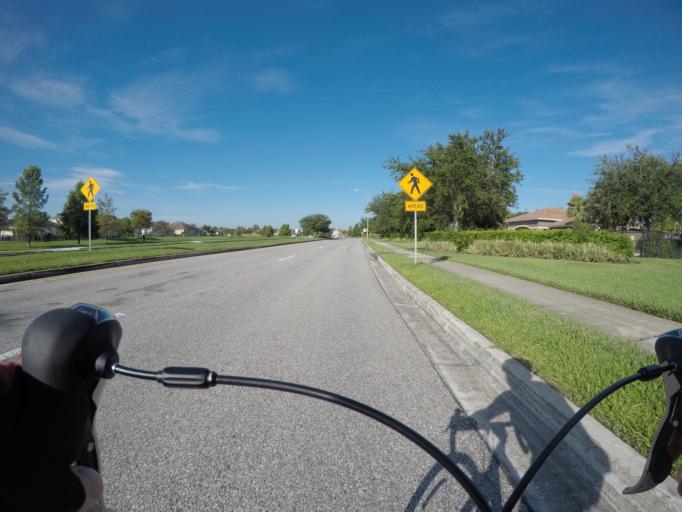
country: US
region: Florida
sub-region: Osceola County
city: Buenaventura Lakes
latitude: 28.3575
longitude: -81.3414
